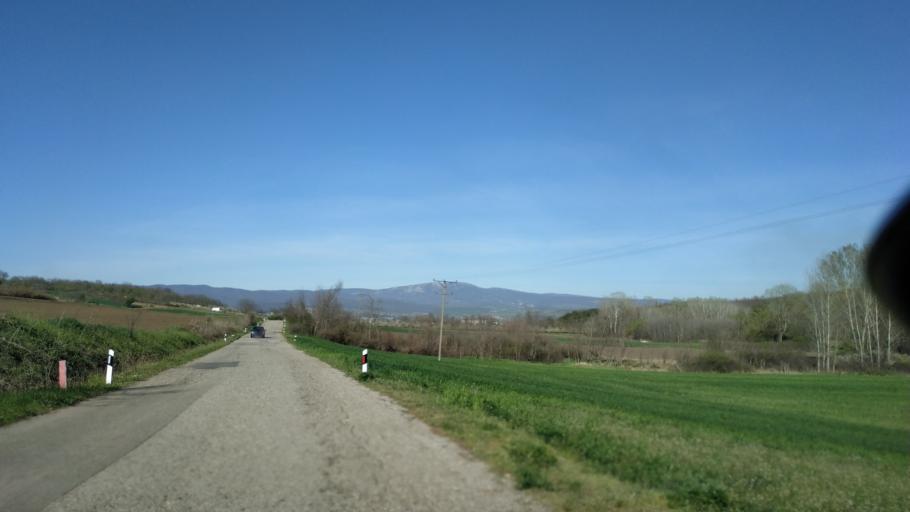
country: RS
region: Central Serbia
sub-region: Nisavski Okrug
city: Aleksinac
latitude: 43.4917
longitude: 21.6693
